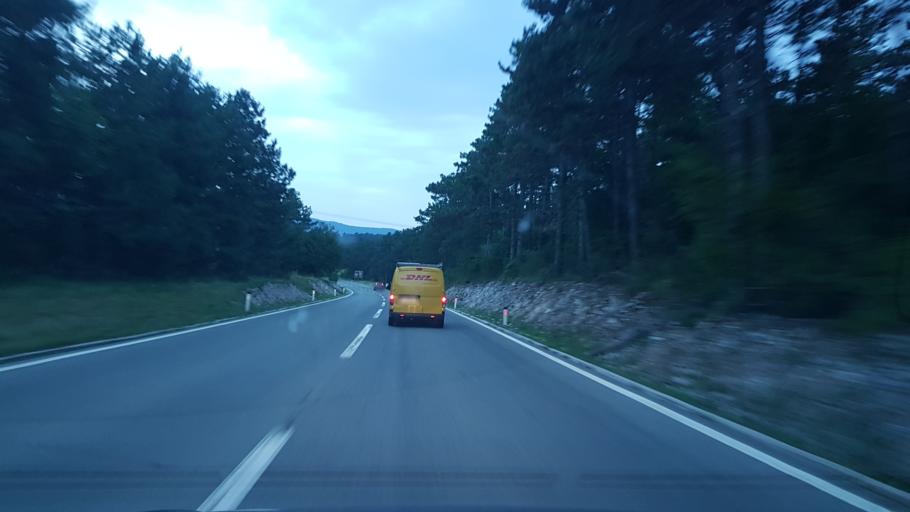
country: SI
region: Divaca
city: Divaca
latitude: 45.6931
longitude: 13.9839
